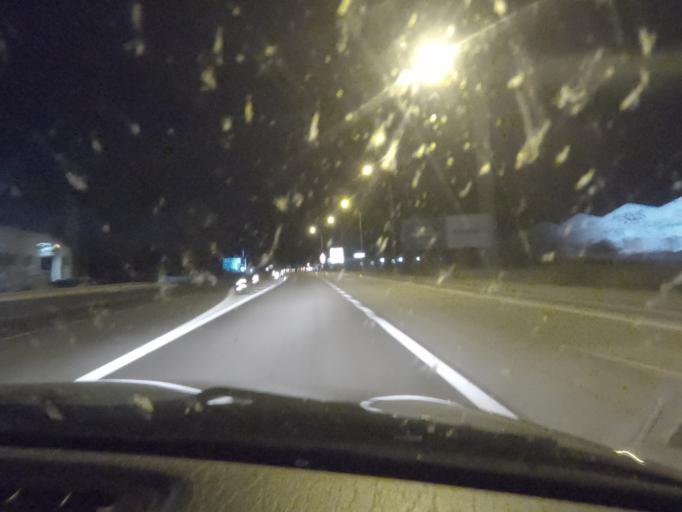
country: ES
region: Extremadura
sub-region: Provincia de Caceres
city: Moraleja
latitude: 40.0585
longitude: -6.6467
